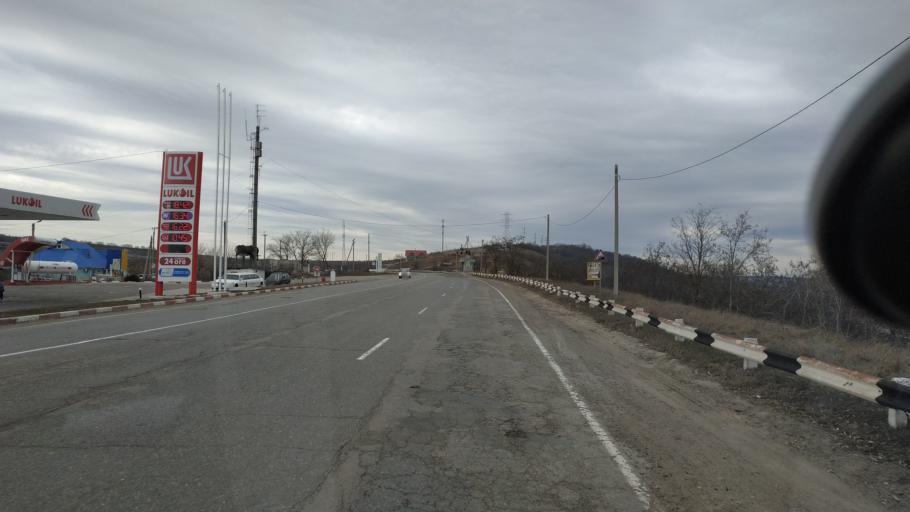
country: MD
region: Chisinau
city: Vadul lui Voda
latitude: 47.0880
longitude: 29.0717
